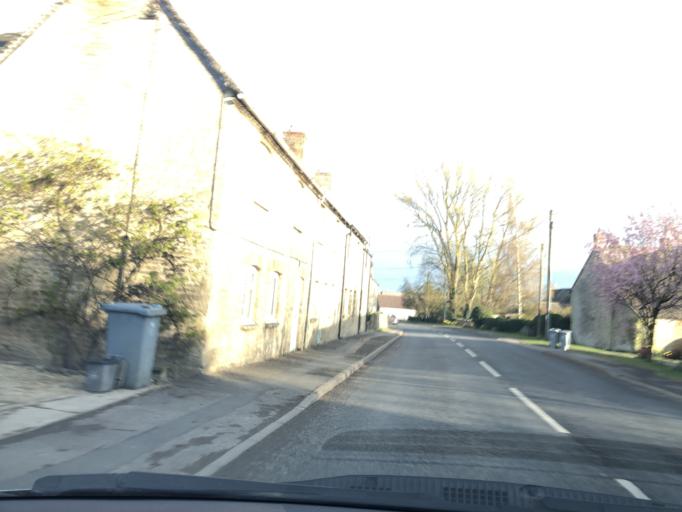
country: GB
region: England
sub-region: Oxfordshire
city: Witney
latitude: 51.7772
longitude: -1.5224
